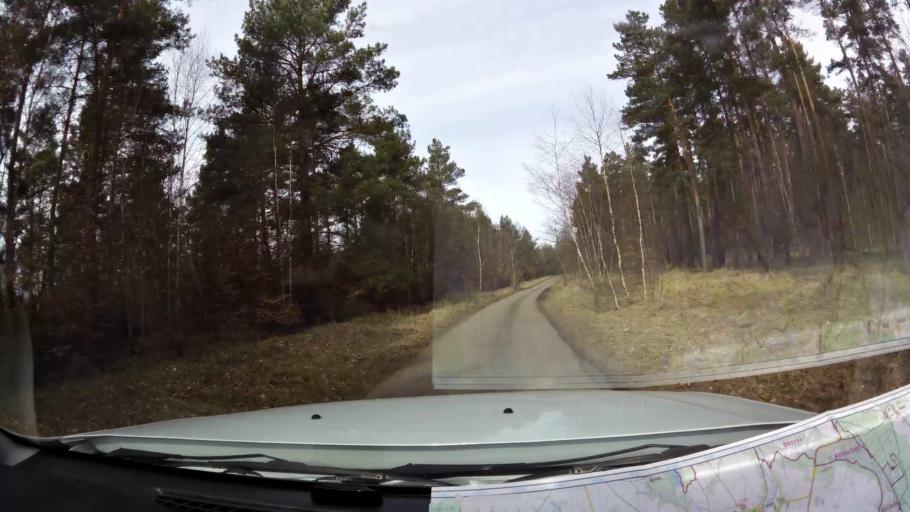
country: PL
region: West Pomeranian Voivodeship
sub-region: Powiat drawski
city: Drawsko Pomorskie
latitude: 53.4774
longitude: 15.6992
